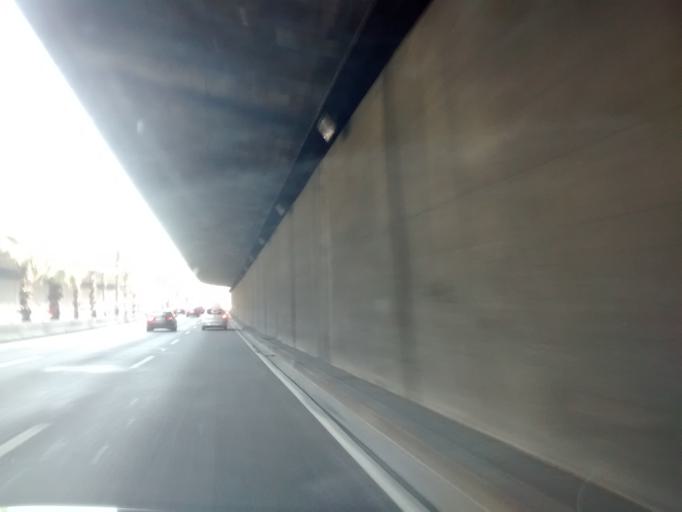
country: ES
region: Catalonia
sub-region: Provincia de Barcelona
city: Sarria-Sant Gervasi
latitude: 41.4225
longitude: 2.1412
